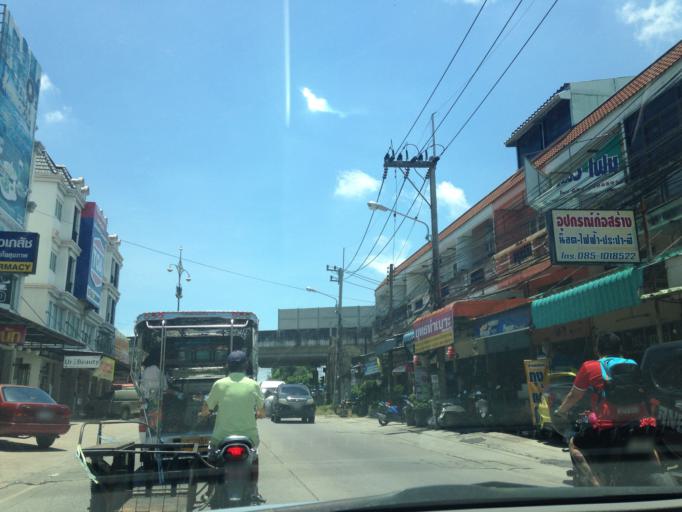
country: TH
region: Chon Buri
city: Chon Buri
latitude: 13.2972
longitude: 100.9357
